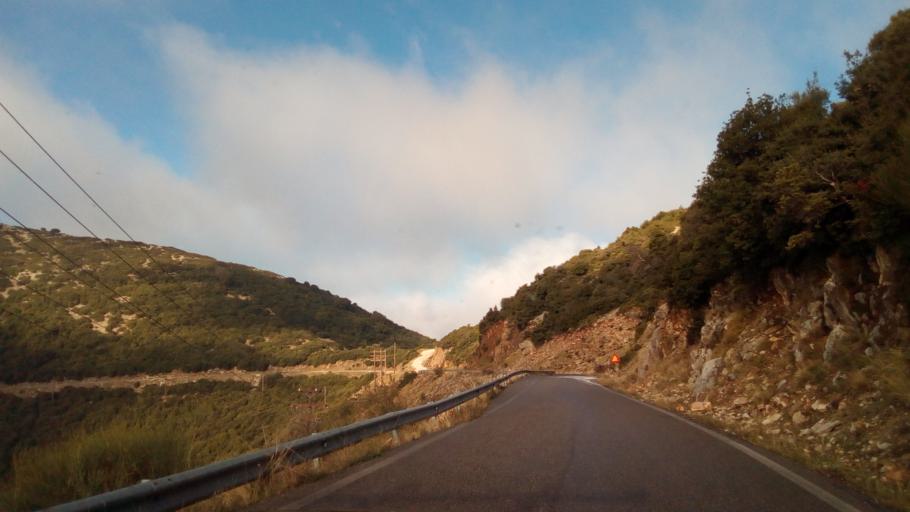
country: GR
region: West Greece
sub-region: Nomos Aitolias kai Akarnanias
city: Thermo
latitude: 38.5838
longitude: 21.7638
